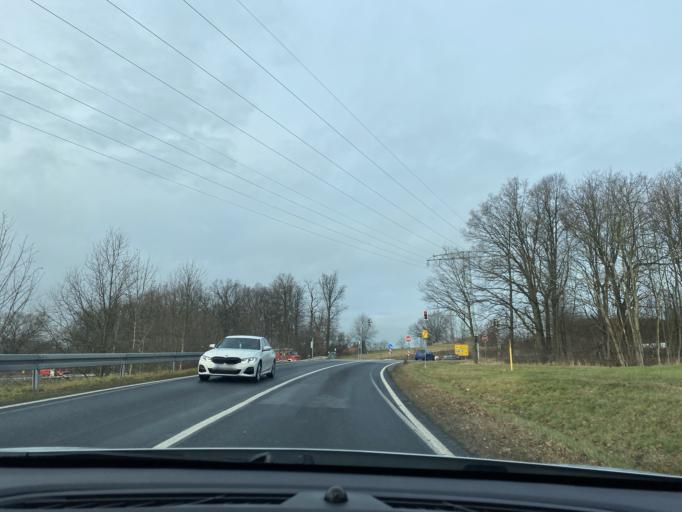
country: DE
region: Saxony
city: Markersdorf
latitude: 51.1478
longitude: 14.9163
